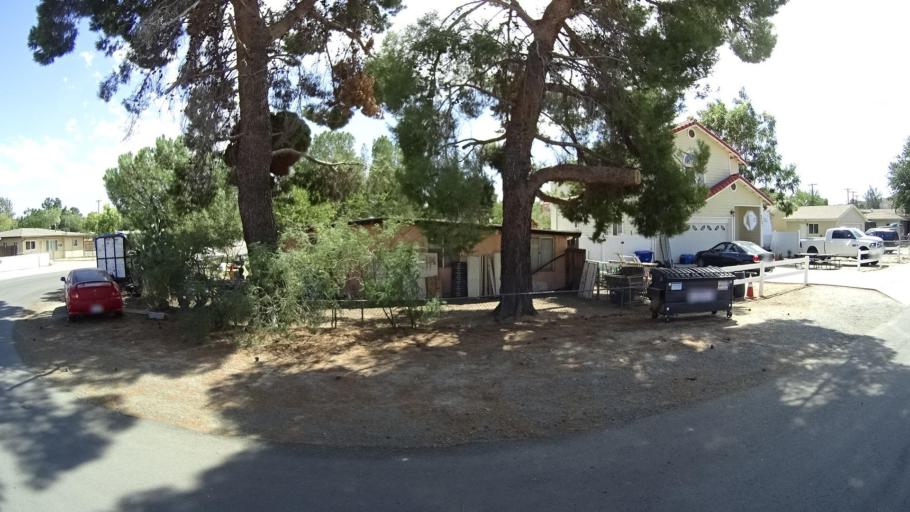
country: MX
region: Baja California
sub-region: Tecate
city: Cereso del Hongo
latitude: 32.6209
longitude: -116.1885
